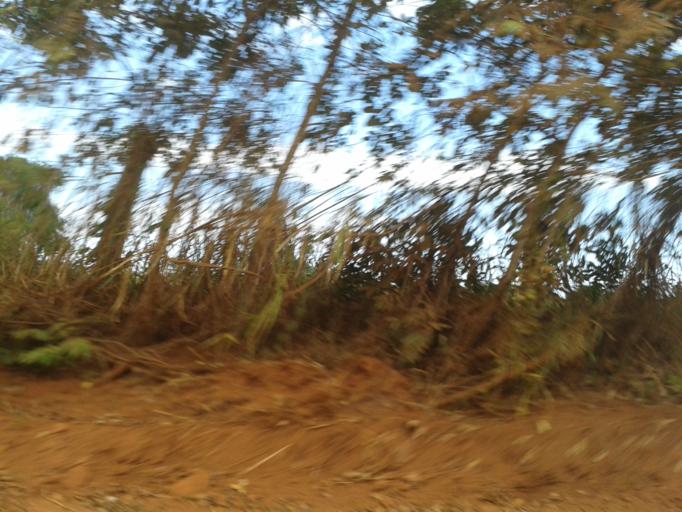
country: BR
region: Minas Gerais
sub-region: Ituiutaba
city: Ituiutaba
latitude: -19.0462
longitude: -49.3687
